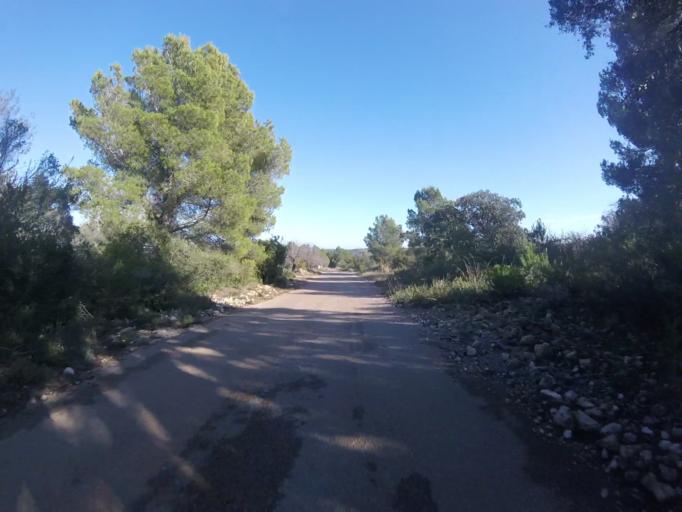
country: ES
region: Valencia
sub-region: Provincia de Castello
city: Cuevas de Vinroma
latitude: 40.2899
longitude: 0.0815
